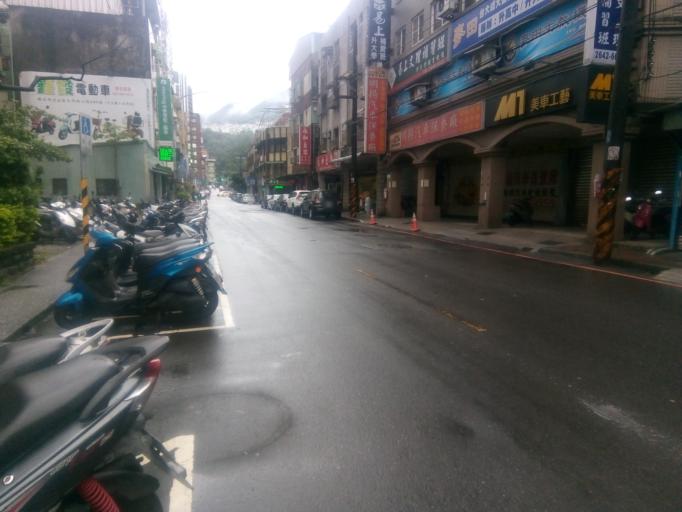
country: TW
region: Taiwan
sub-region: Keelung
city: Keelung
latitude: 25.0655
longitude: 121.6622
